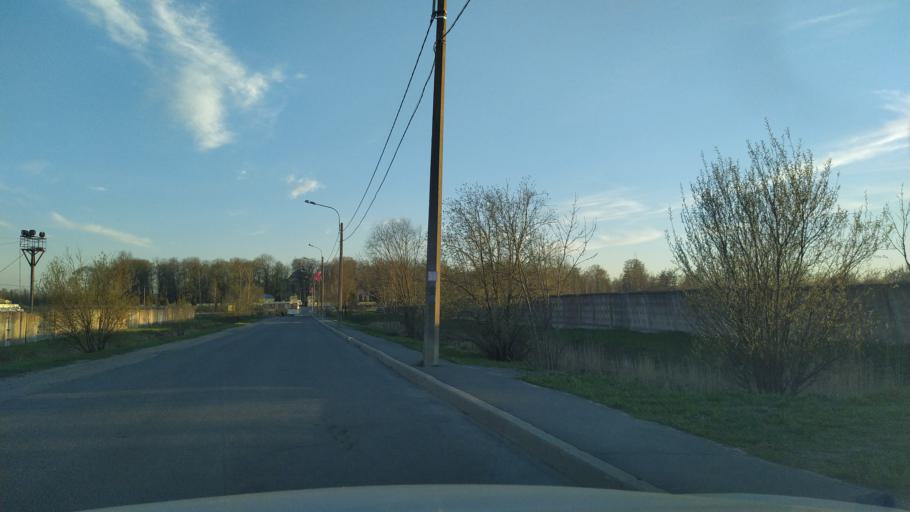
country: RU
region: St.-Petersburg
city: Pushkin
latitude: 59.6969
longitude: 30.3908
